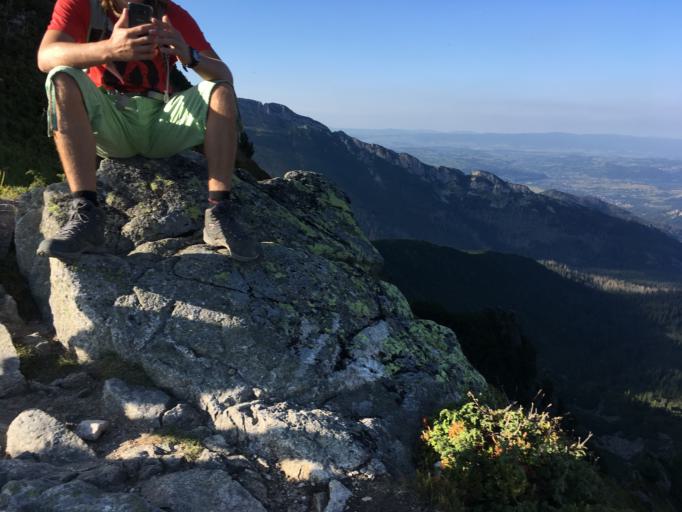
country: PL
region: Lesser Poland Voivodeship
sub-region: Powiat tatrzanski
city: Zakopane
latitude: 49.2333
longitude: 19.9465
